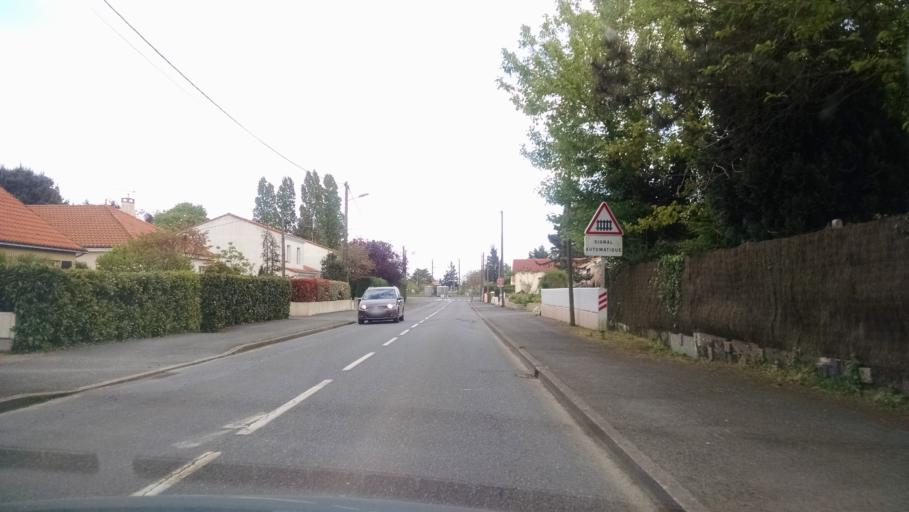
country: FR
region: Pays de la Loire
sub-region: Departement de la Loire-Atlantique
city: Gorges
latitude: 47.0909
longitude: -1.2957
